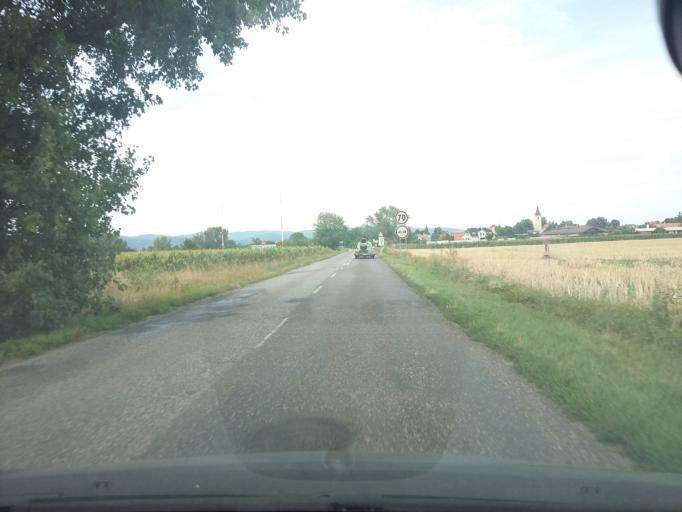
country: SK
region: Bratislavsky
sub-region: Okres Pezinok
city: Pezinok
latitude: 48.2226
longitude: 17.2912
